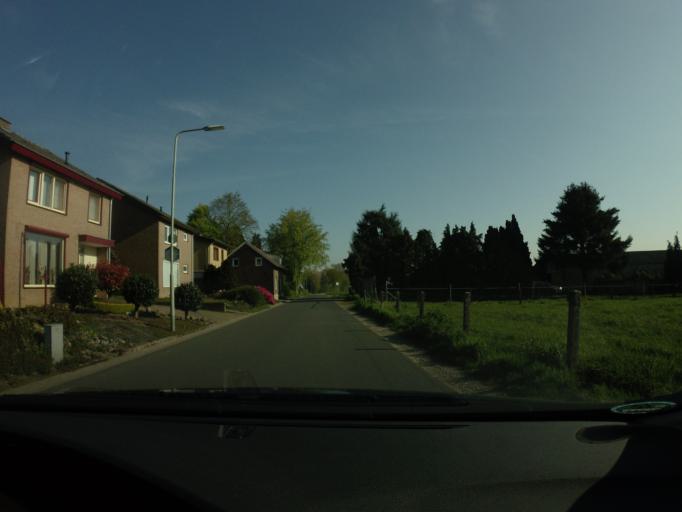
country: NL
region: Limburg
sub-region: Gemeente Stein
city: Elsloo
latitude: 50.9285
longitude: 5.7606
